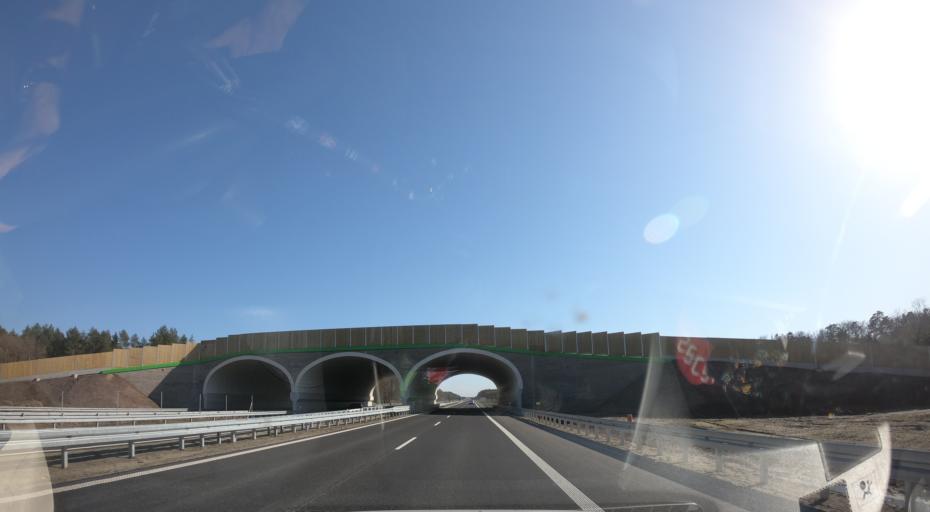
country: PL
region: West Pomeranian Voivodeship
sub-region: Powiat goleniowski
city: Przybiernow
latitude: 53.6669
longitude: 14.8139
